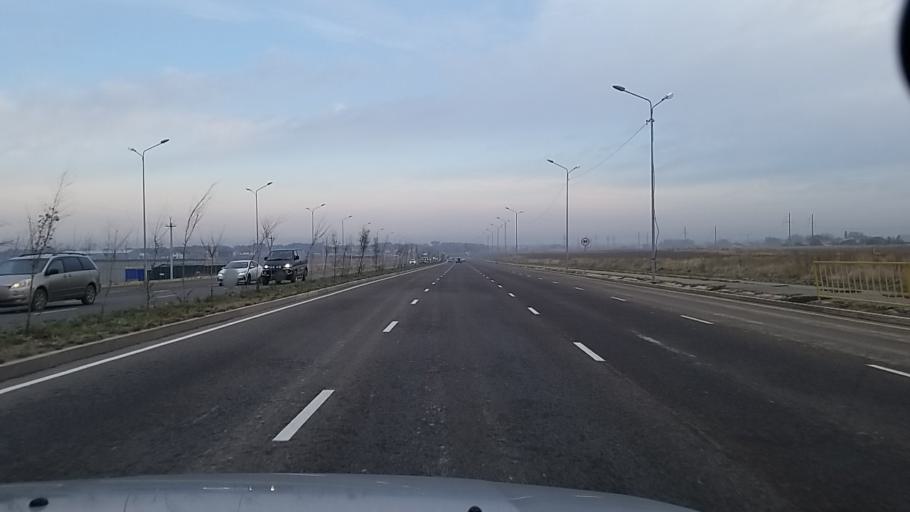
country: KZ
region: Almaty Oblysy
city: Burunday
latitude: 43.3422
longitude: 76.8338
